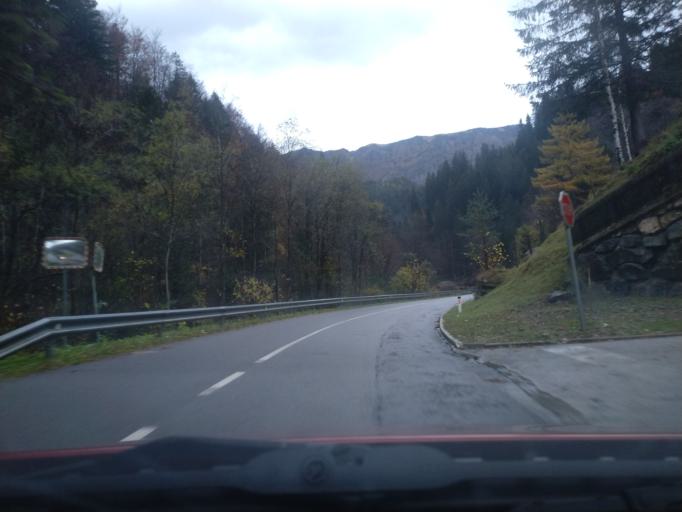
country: SI
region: Solcava
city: Solcava
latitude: 46.4135
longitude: 14.7004
